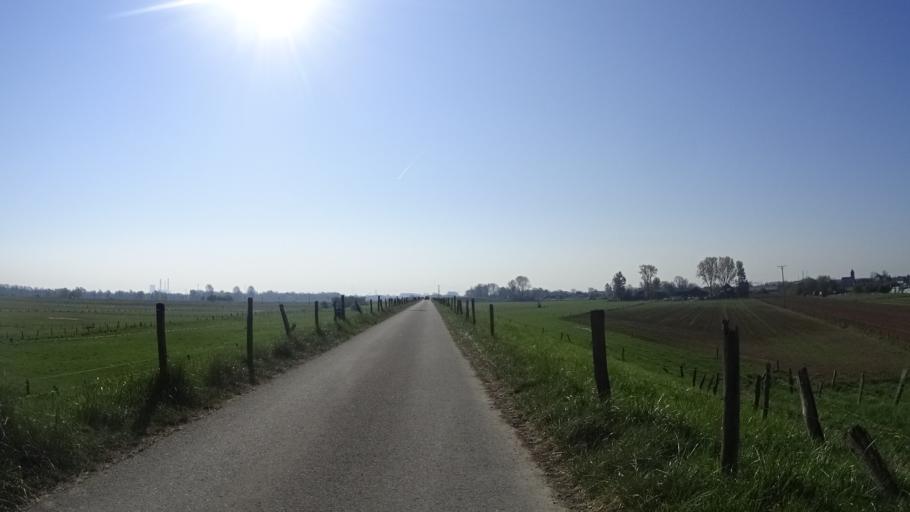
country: DE
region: North Rhine-Westphalia
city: Rheinberg
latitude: 51.6027
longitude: 6.5777
